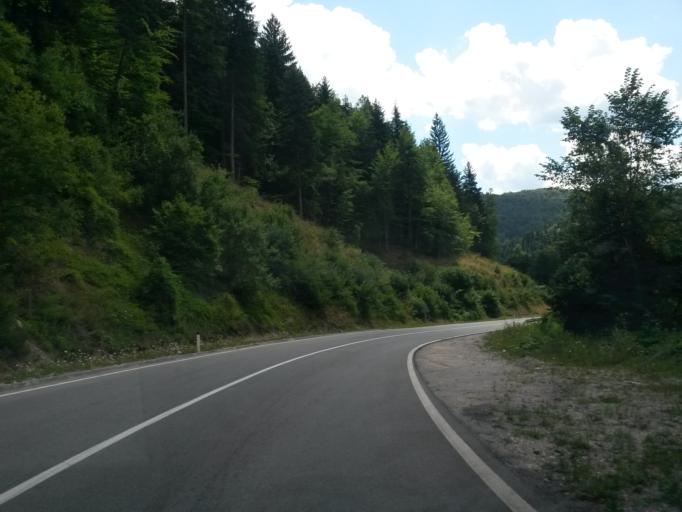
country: BA
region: Federation of Bosnia and Herzegovina
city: Bugojno
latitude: 44.0298
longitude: 17.3533
